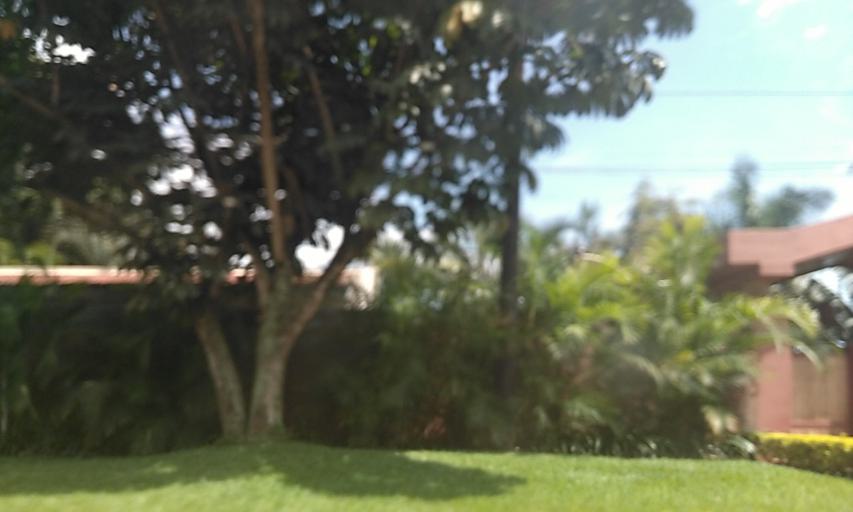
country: UG
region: Central Region
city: Kampala Central Division
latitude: 0.3358
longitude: 32.5955
